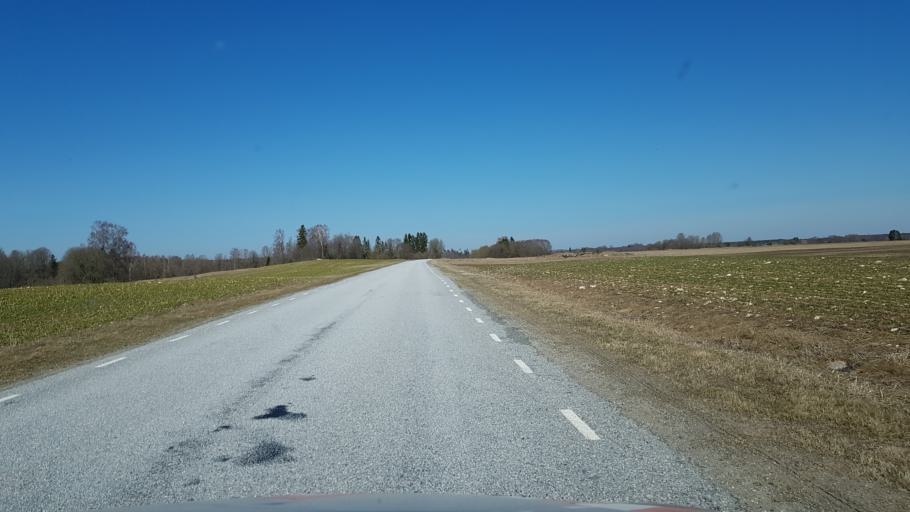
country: EE
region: Jaervamaa
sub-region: Koeru vald
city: Koeru
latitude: 59.0112
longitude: 26.0890
